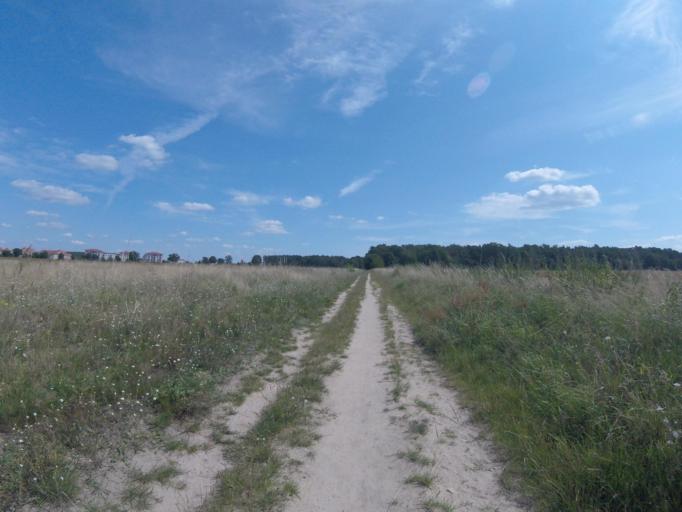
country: DE
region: Brandenburg
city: Wildau
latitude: 52.3266
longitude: 13.6051
